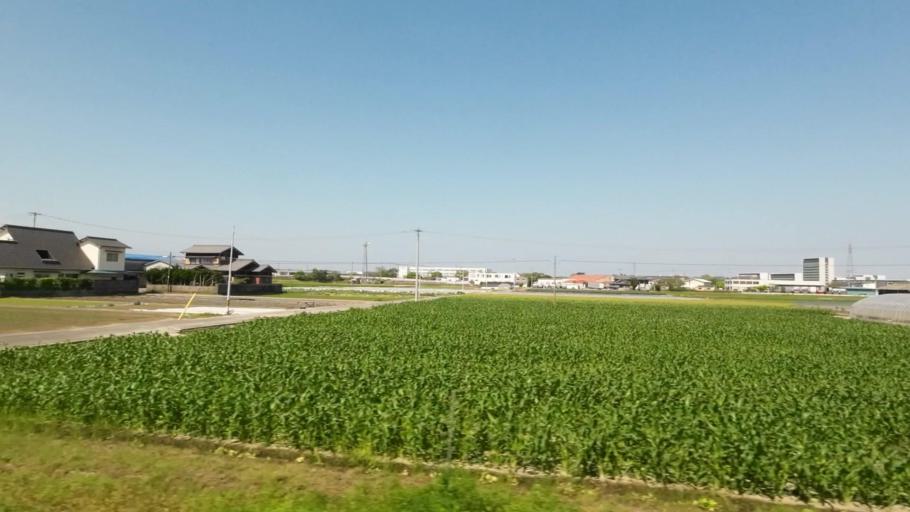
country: JP
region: Kagawa
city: Kan'onjicho
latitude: 34.1121
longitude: 133.6490
